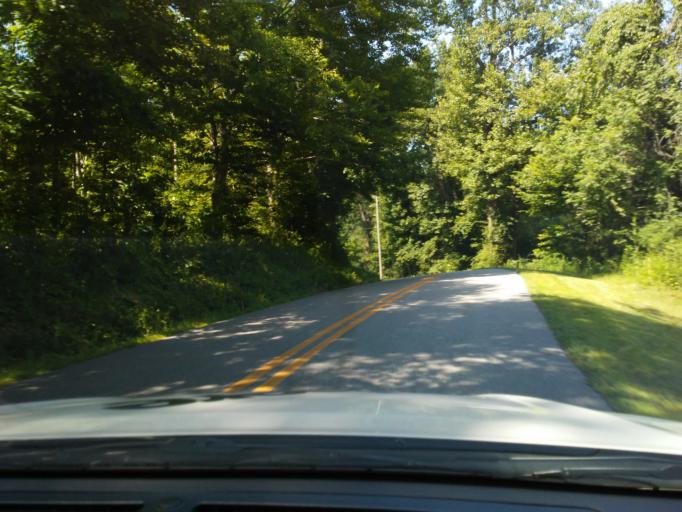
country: US
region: Georgia
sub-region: Union County
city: Blairsville
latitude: 34.9259
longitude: -83.8664
